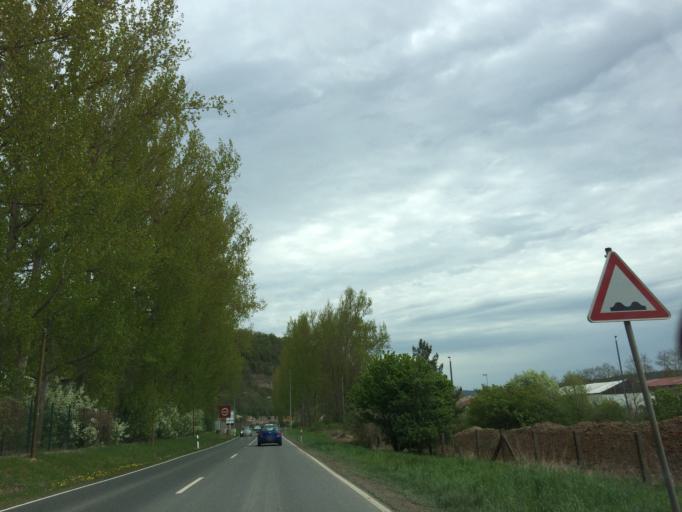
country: DE
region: Thuringia
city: Schops
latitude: 50.8383
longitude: 11.5934
